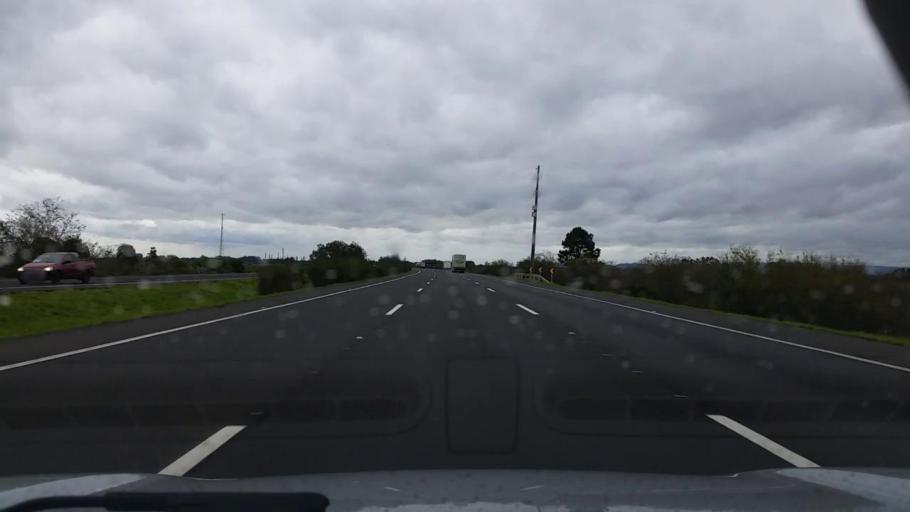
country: BR
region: Rio Grande do Sul
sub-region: Rolante
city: Rolante
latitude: -29.8862
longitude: -50.6593
